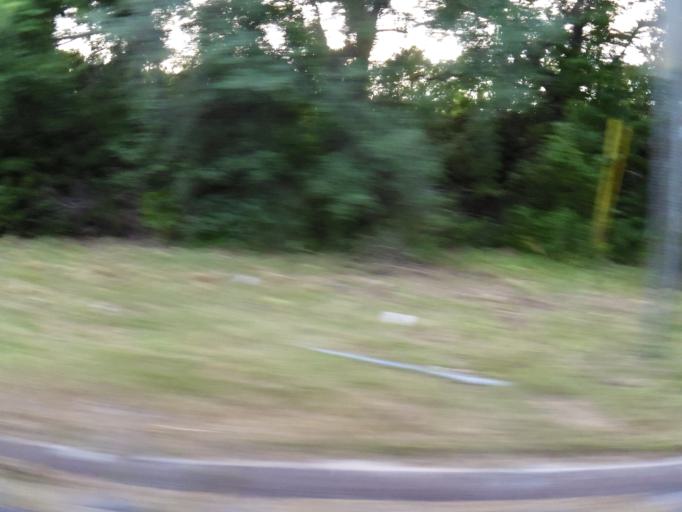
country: US
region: Florida
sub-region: Duval County
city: Jacksonville
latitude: 30.2994
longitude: -81.6126
